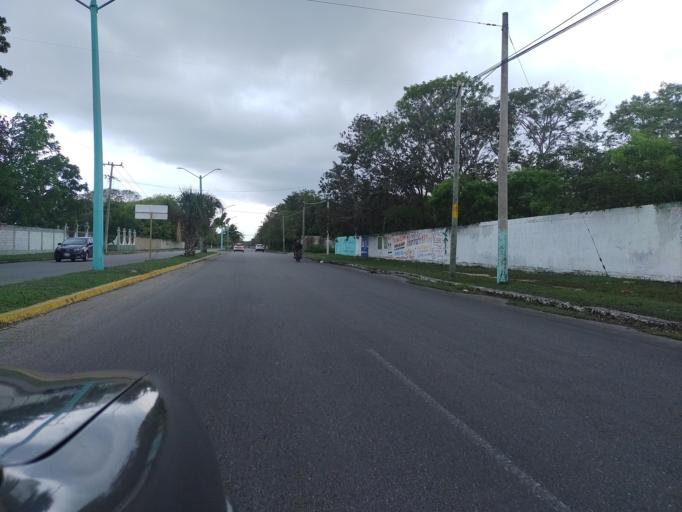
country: MX
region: Quintana Roo
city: Chetumal
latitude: 18.5116
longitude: -88.2810
